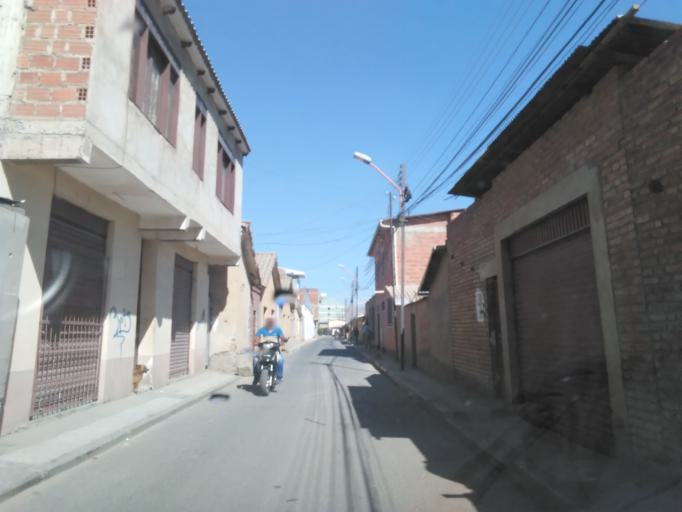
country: BO
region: Cochabamba
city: Cochabamba
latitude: -17.4133
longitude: -66.1551
